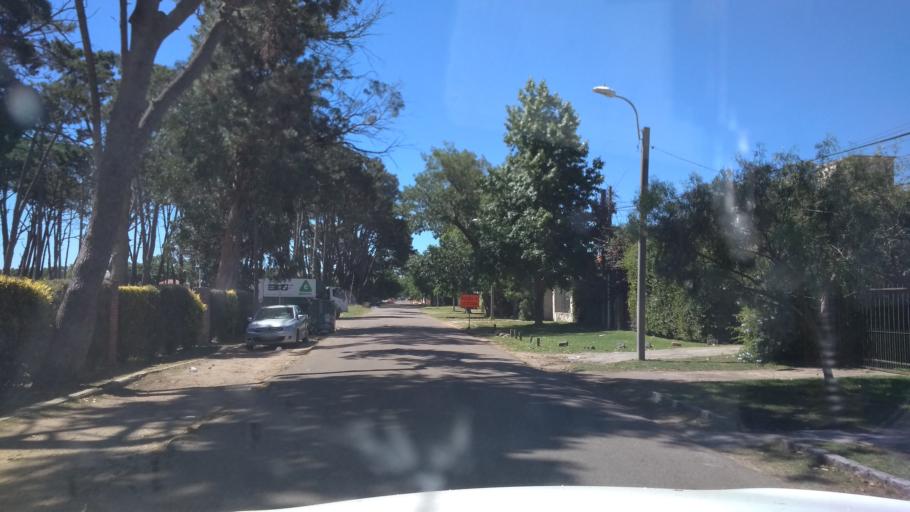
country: UY
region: Canelones
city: Paso de Carrasco
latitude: -34.8748
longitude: -56.0609
